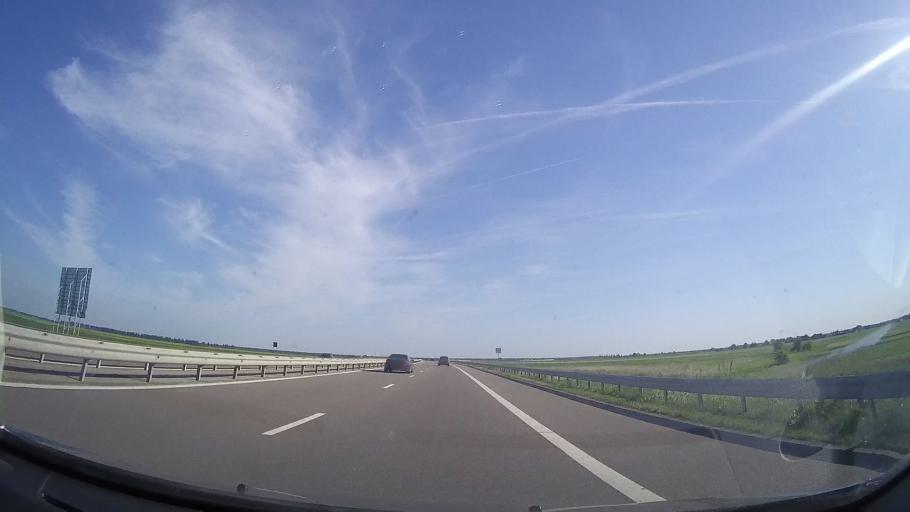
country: RO
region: Ilfov
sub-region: Comuna Gruiu
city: Gruiu
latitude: 44.7463
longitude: 26.2561
